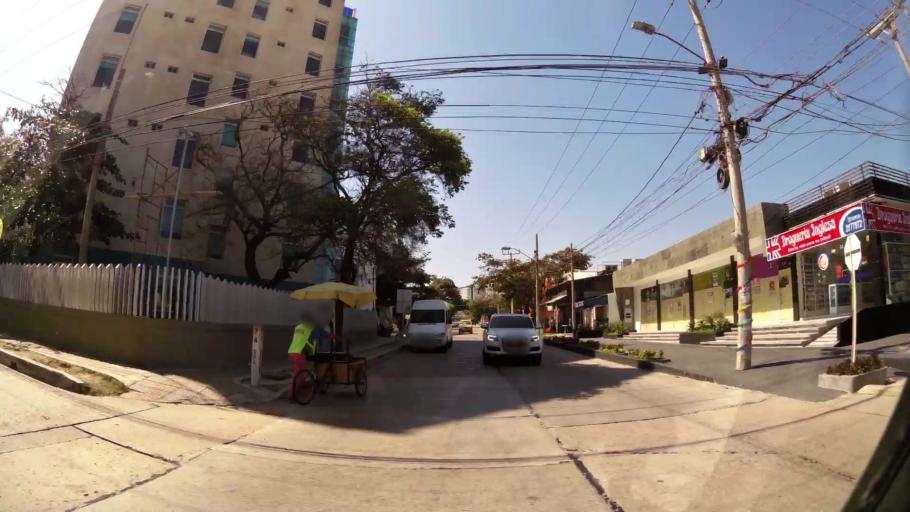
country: CO
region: Atlantico
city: Barranquilla
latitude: 11.0147
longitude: -74.7965
